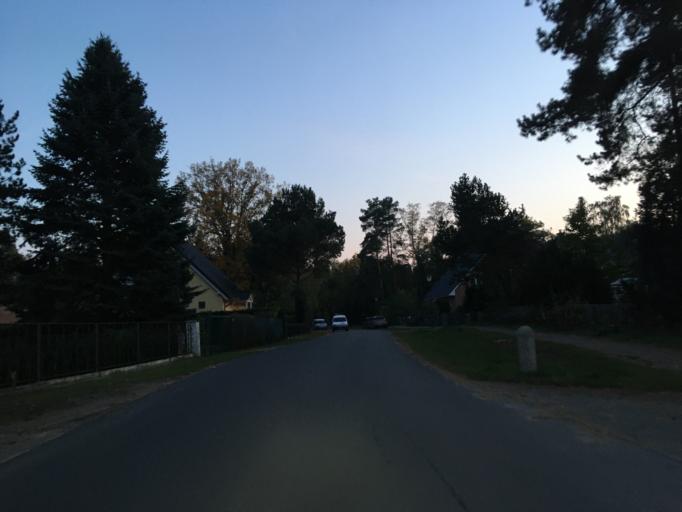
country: DE
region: Brandenburg
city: Birkenwerder
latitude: 52.6793
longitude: 13.3211
